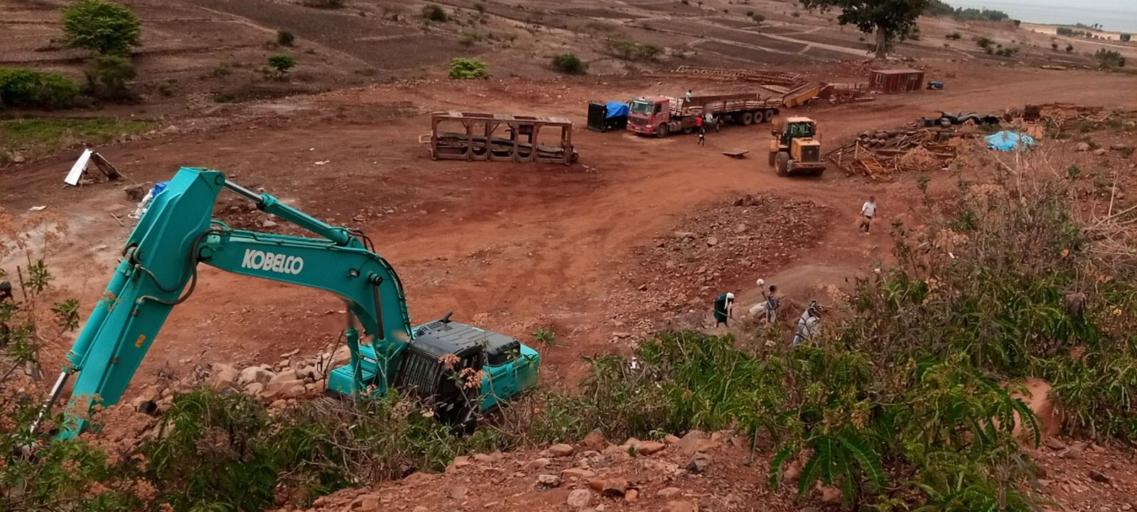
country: ET
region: Amhara
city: Bahir Dar
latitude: 11.8698
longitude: 36.9990
